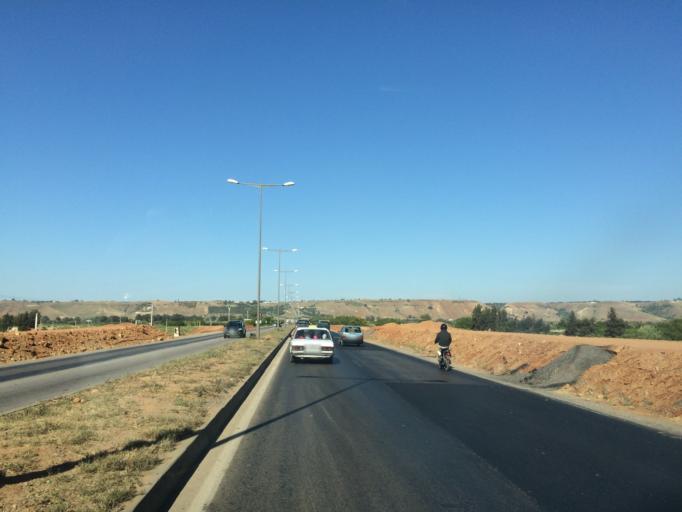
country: MA
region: Rabat-Sale-Zemmour-Zaer
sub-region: Rabat
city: Rabat
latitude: 33.9870
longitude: -6.7875
